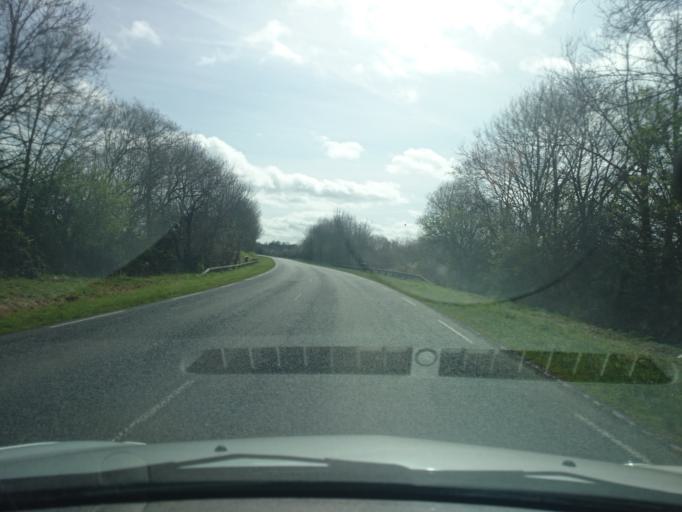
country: FR
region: Brittany
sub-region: Departement du Finistere
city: Gouesnou
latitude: 48.4389
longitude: -4.4551
